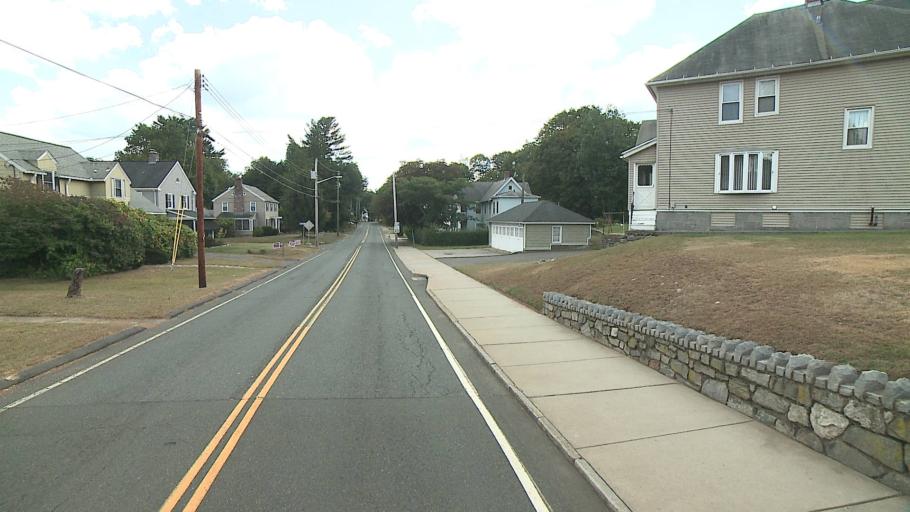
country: US
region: Connecticut
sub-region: New Haven County
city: Ansonia
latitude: 41.3522
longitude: -73.0906
